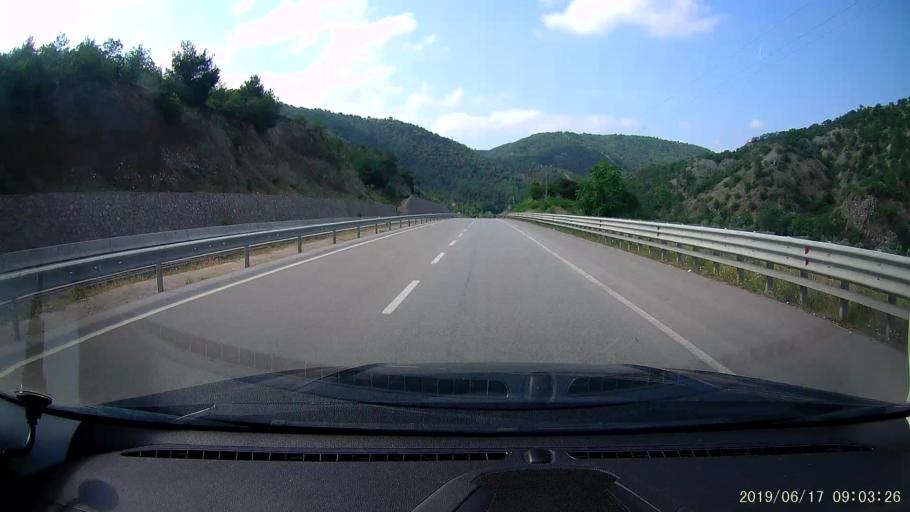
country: TR
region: Amasya
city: Tasova
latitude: 40.7555
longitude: 36.3023
